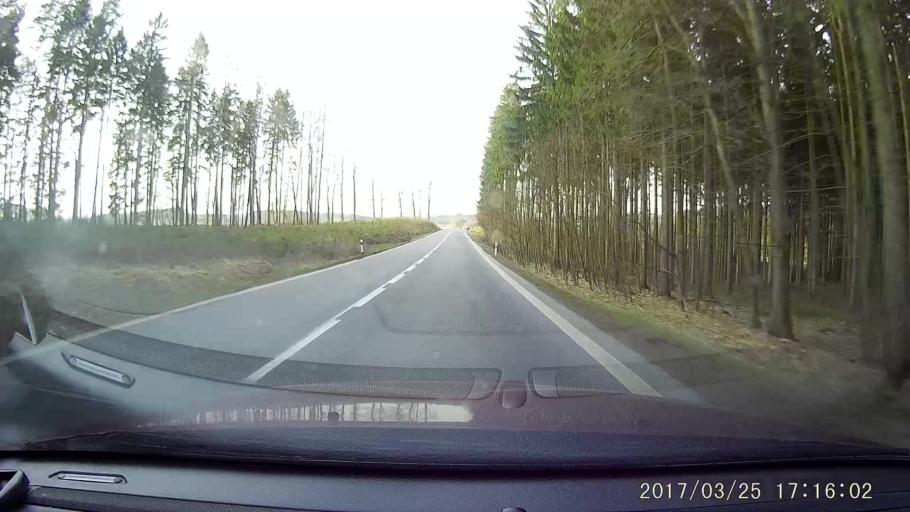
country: CZ
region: Liberecky
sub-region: Okres Liberec
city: Frydlant
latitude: 50.9525
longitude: 15.0955
